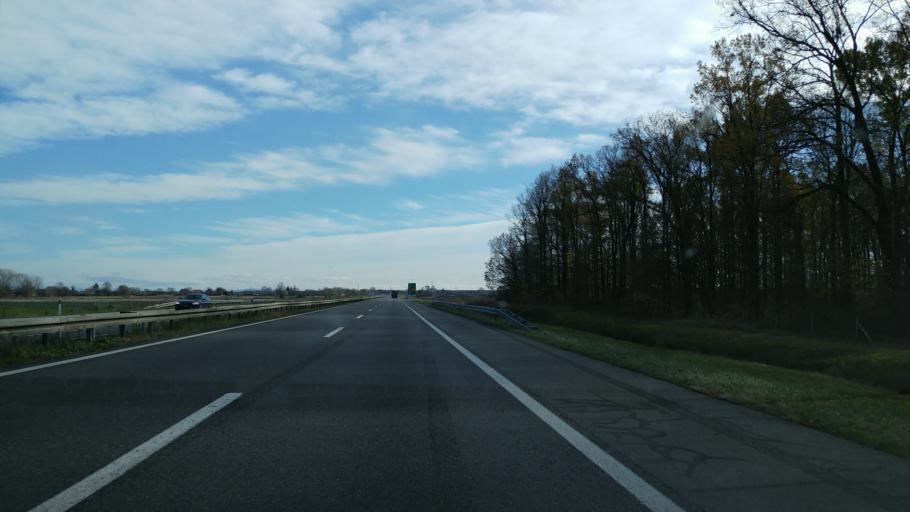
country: HR
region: Sisacko-Moslavacka
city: Repusnica
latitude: 45.4693
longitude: 16.7432
